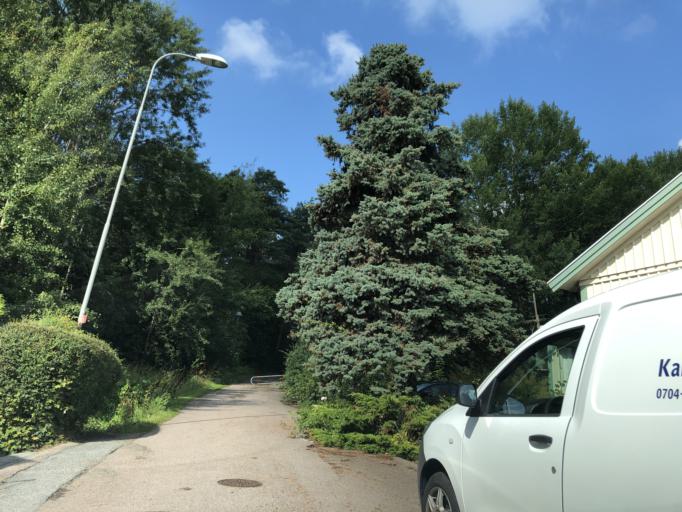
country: SE
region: Vaestra Goetaland
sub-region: Goteborg
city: Majorna
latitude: 57.7188
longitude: 11.8985
